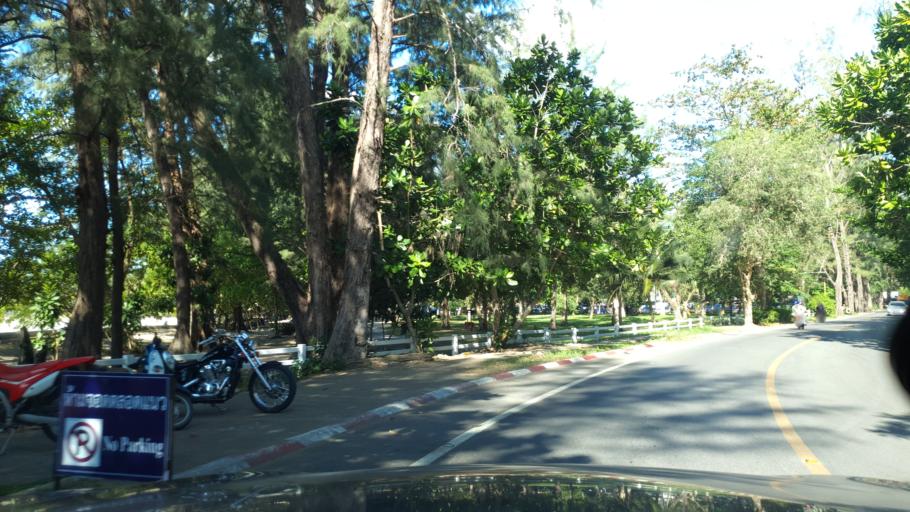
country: TH
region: Phangnga
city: Ban Ao Nang
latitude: 8.0461
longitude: 98.8024
